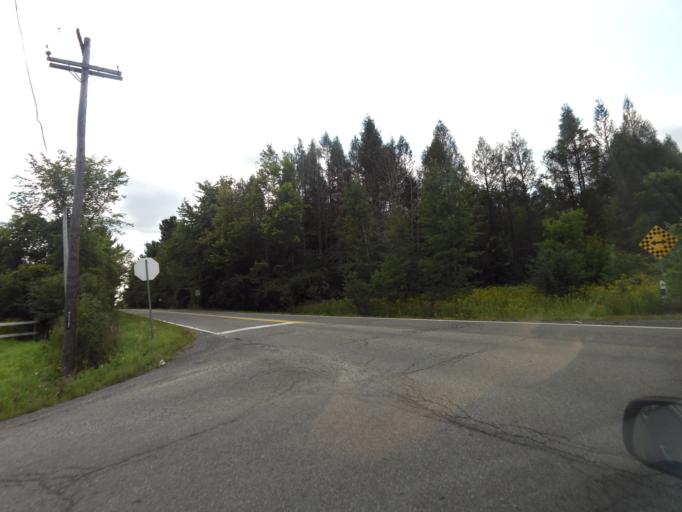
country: CA
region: Ontario
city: Ottawa
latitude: 45.3960
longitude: -75.5818
